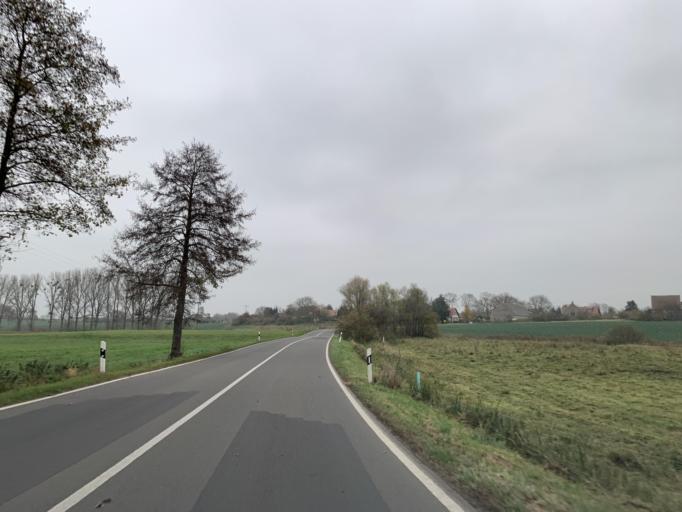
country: DE
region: Mecklenburg-Vorpommern
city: Blankensee
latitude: 53.4157
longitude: 13.2517
